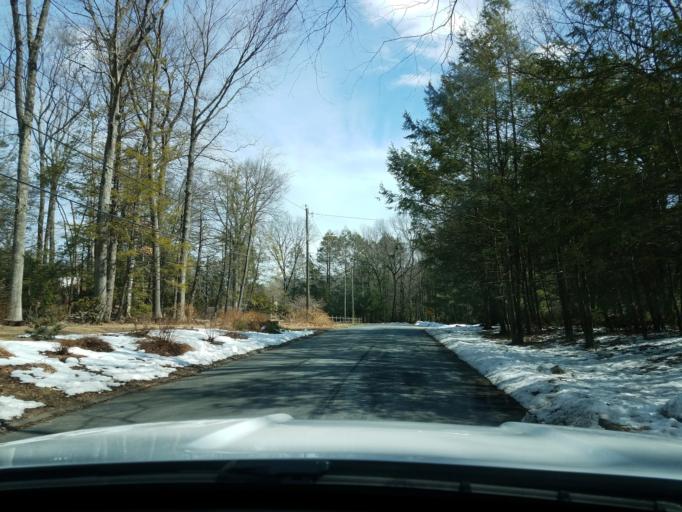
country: US
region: Connecticut
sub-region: Hartford County
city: Canton Valley
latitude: 41.7851
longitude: -72.8720
